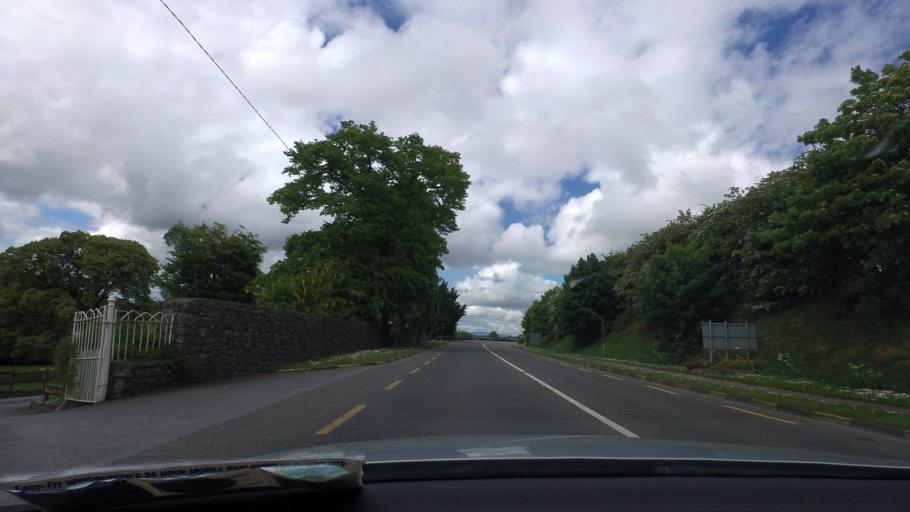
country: IE
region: Munster
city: Cashel
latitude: 52.5218
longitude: -7.8869
